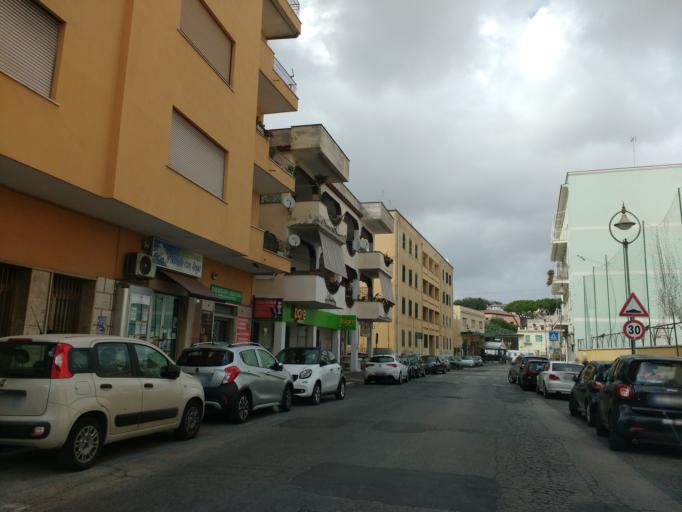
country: IT
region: Latium
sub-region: Citta metropolitana di Roma Capitale
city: Anzio
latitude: 41.4476
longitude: 12.6276
